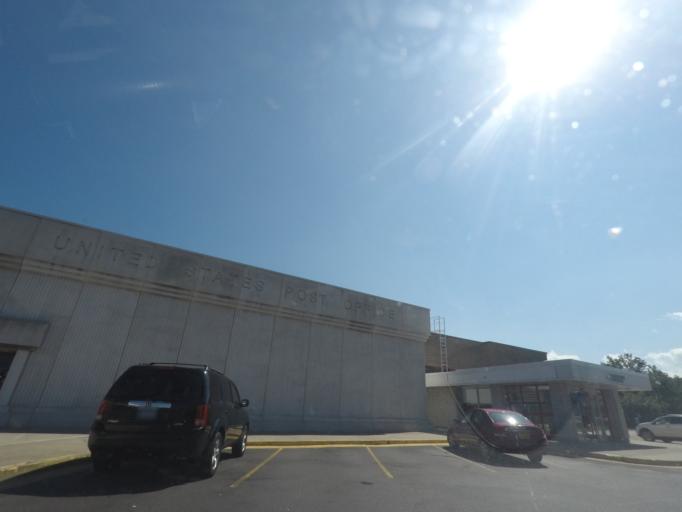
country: US
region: New York
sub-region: Albany County
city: Colonie
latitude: 42.7285
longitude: -73.8483
